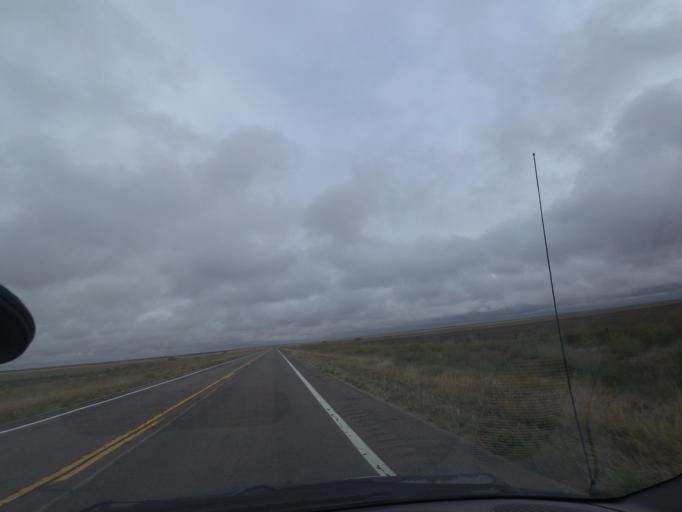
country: US
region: Colorado
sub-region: Washington County
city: Akron
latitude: 39.7357
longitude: -103.1718
